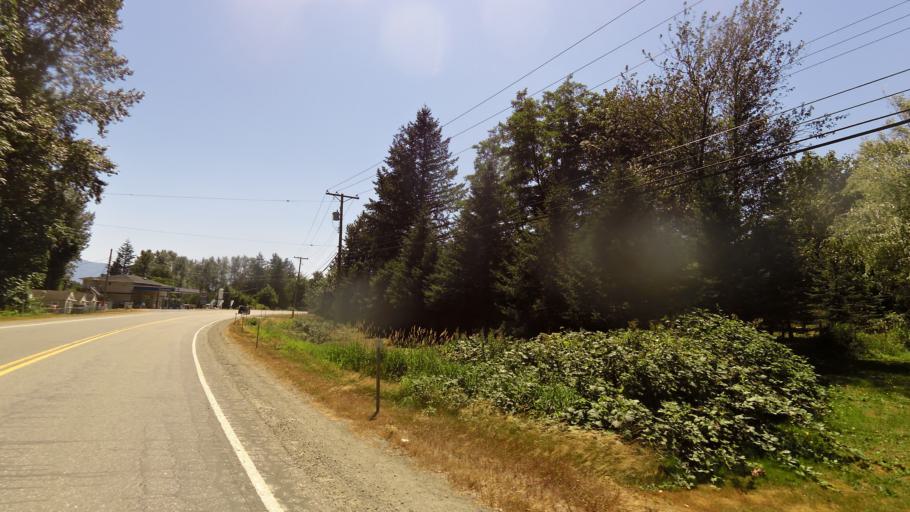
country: CA
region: British Columbia
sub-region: Fraser Valley Regional District
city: Chilliwack
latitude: 49.2210
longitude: -122.0113
